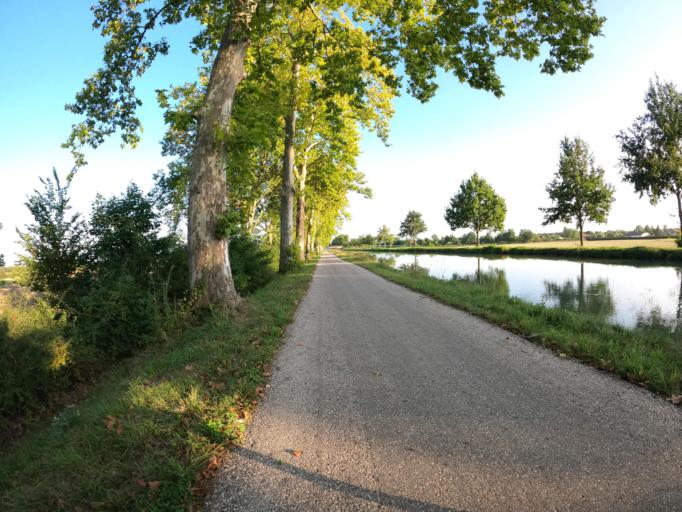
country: FR
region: Midi-Pyrenees
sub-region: Departement du Tarn-et-Garonne
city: Saint-Porquier
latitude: 44.0178
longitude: 1.1700
